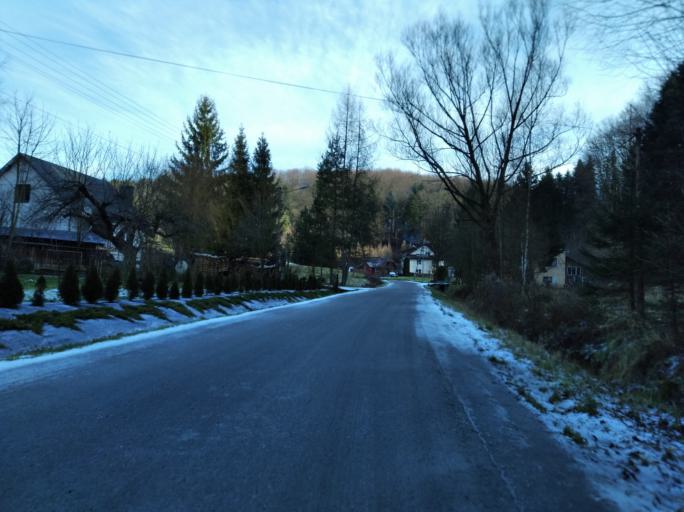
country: PL
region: Subcarpathian Voivodeship
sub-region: Powiat strzyzowski
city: Strzyzow
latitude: 49.8908
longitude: 21.7756
